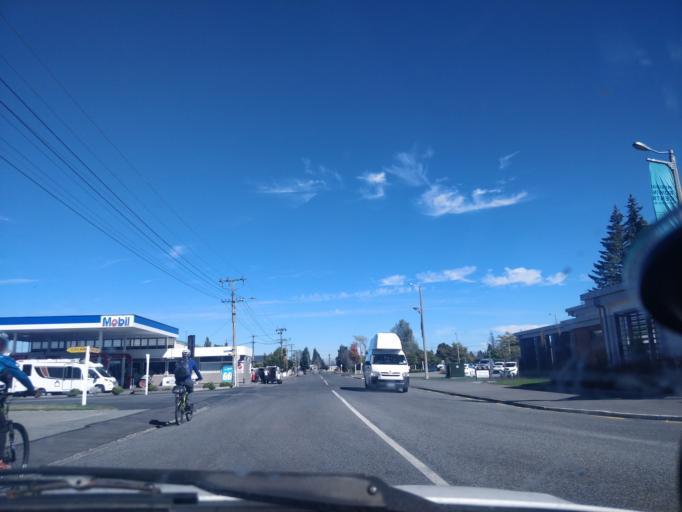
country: NZ
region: Canterbury
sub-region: Timaru District
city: Pleasant Point
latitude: -44.2574
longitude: 170.1003
